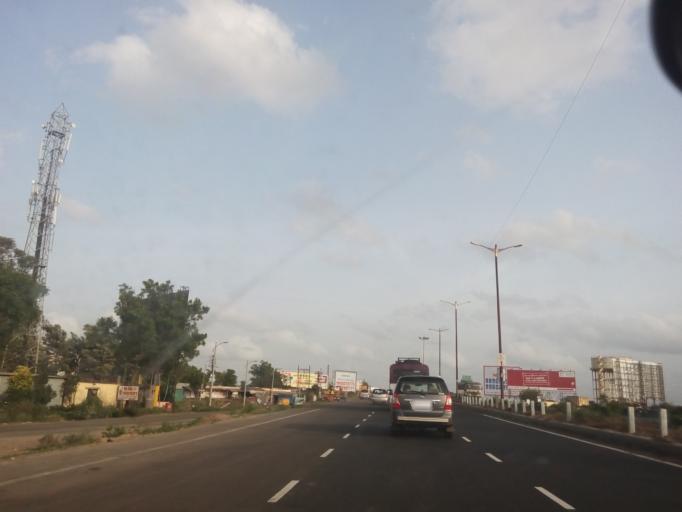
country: IN
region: Maharashtra
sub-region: Pune Division
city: Pimpri
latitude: 18.6359
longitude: 73.7403
